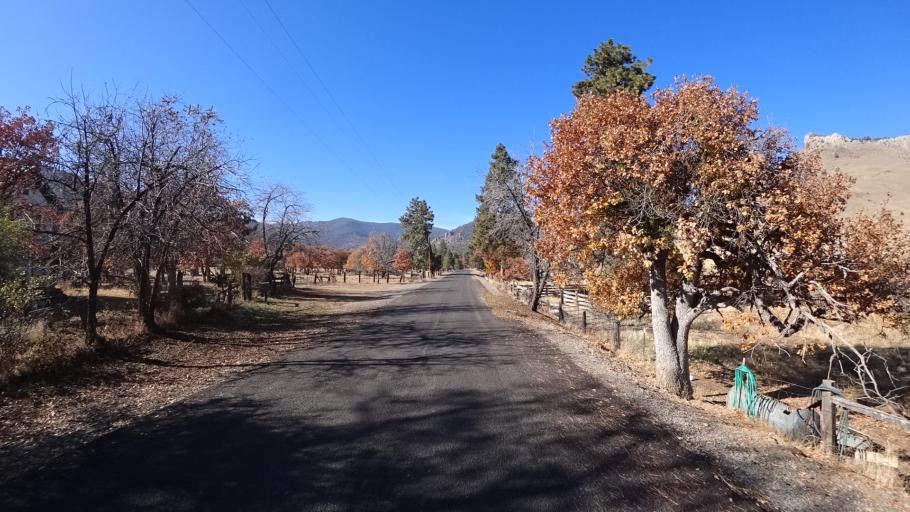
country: US
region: California
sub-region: Siskiyou County
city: Weed
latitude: 41.5033
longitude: -122.5699
